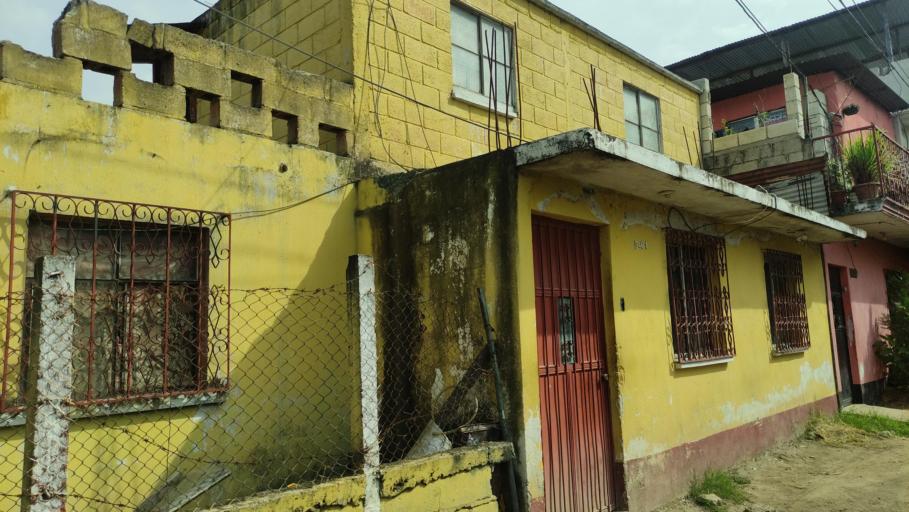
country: GT
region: Guatemala
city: Villa Canales
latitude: 14.4883
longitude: -90.5372
